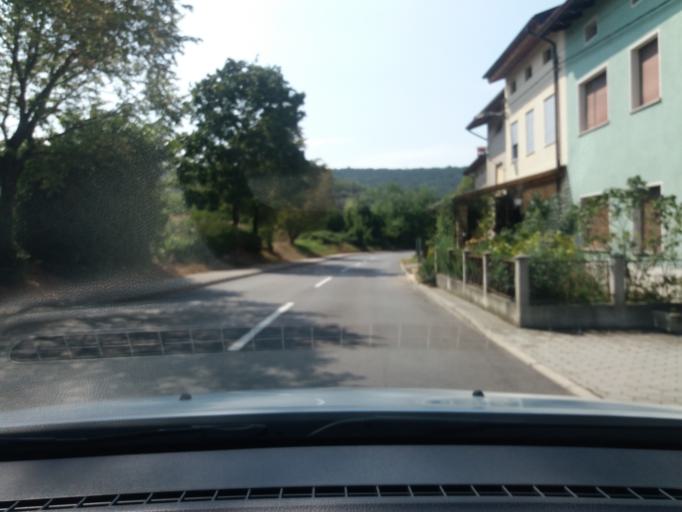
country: SI
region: Miren-Kostanjevica
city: Miren
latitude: 45.8897
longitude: 13.6033
